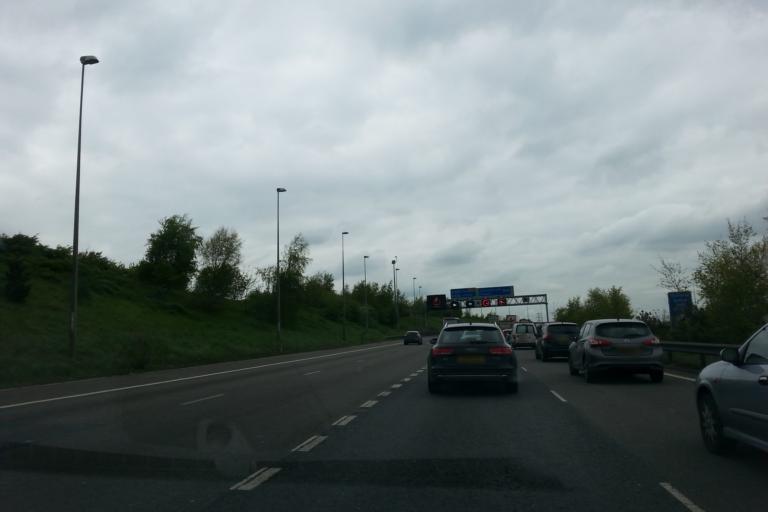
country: GB
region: England
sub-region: Warwickshire
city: Curdworth
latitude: 52.5307
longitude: -1.7300
